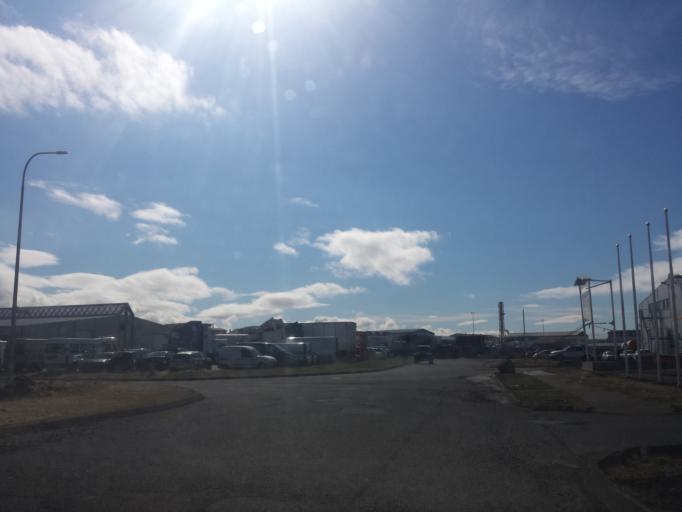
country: IS
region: Capital Region
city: Gardabaer
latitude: 64.0810
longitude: -21.9300
